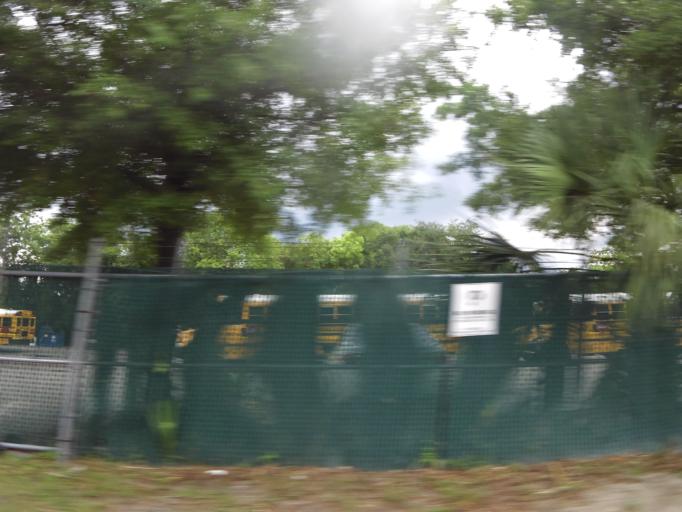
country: US
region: Florida
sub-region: Duval County
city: Jacksonville
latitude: 30.3288
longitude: -81.5366
